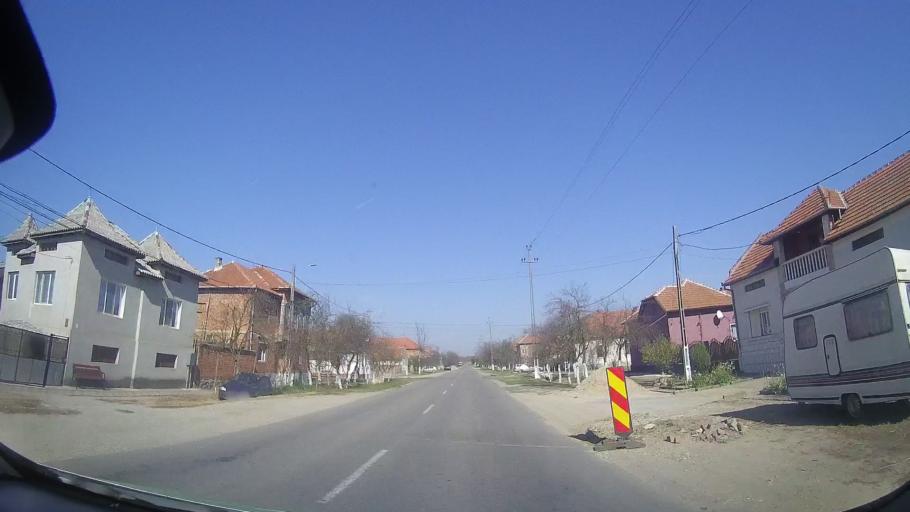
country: RO
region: Timis
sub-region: Comuna Costeiu
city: Costeiu
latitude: 45.7439
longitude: 21.8479
